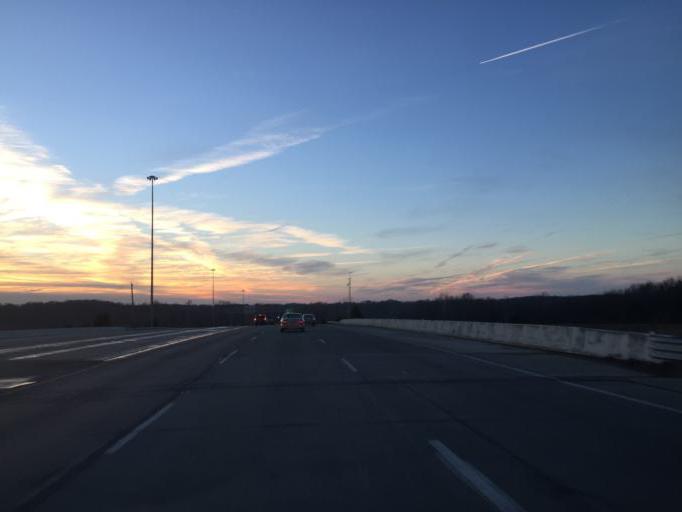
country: US
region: Indiana
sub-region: Monroe County
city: Bloomington
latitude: 39.1872
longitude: -86.5543
